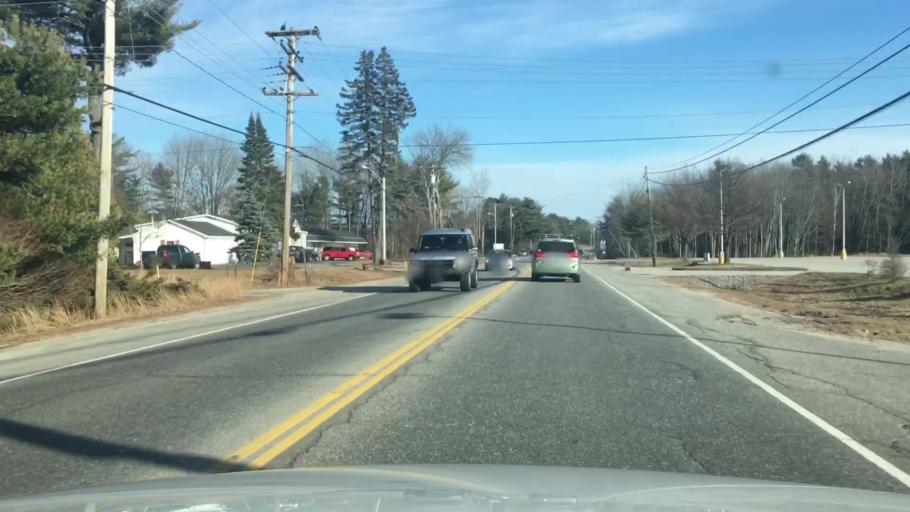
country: US
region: Maine
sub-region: Cumberland County
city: Brunswick
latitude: 43.9110
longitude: -69.9014
